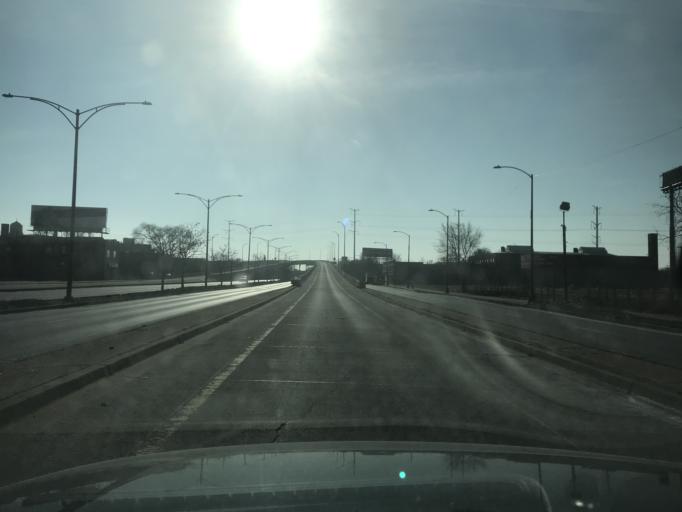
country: US
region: Illinois
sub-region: Cook County
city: Chicago
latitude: 41.7550
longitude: -87.5861
